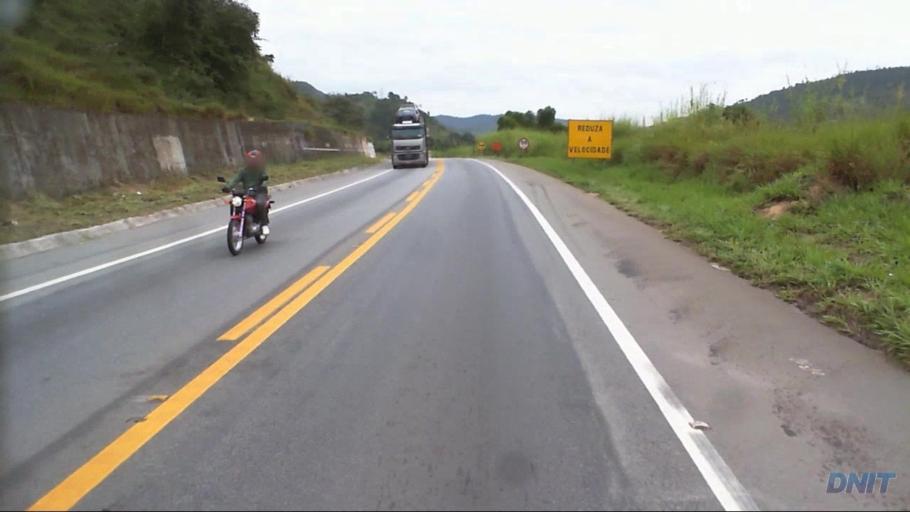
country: BR
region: Minas Gerais
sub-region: Timoteo
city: Timoteo
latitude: -19.6032
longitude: -42.7570
